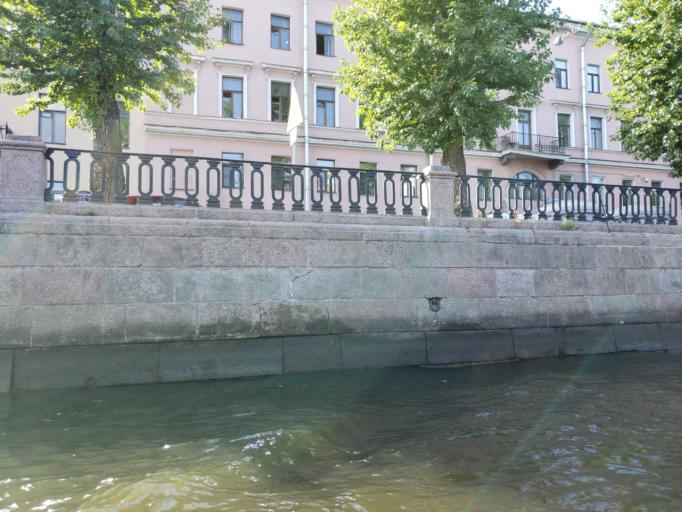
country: RU
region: St.-Petersburg
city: Admiralteisky
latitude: 59.9217
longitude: 30.2981
